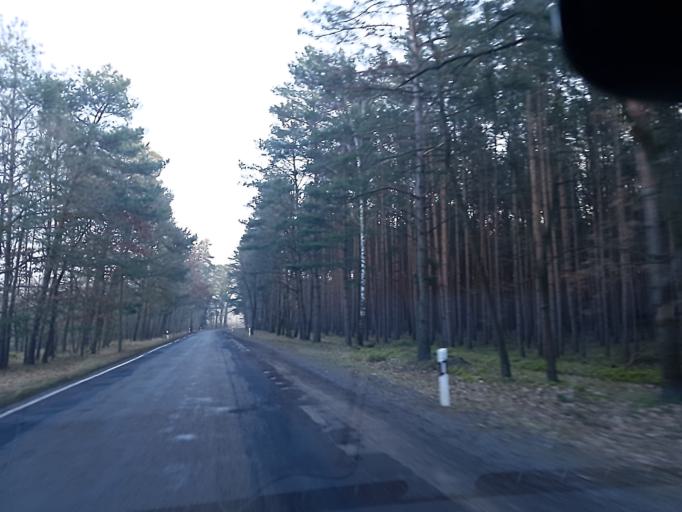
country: DE
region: Brandenburg
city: Gorzke
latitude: 52.1948
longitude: 12.3872
